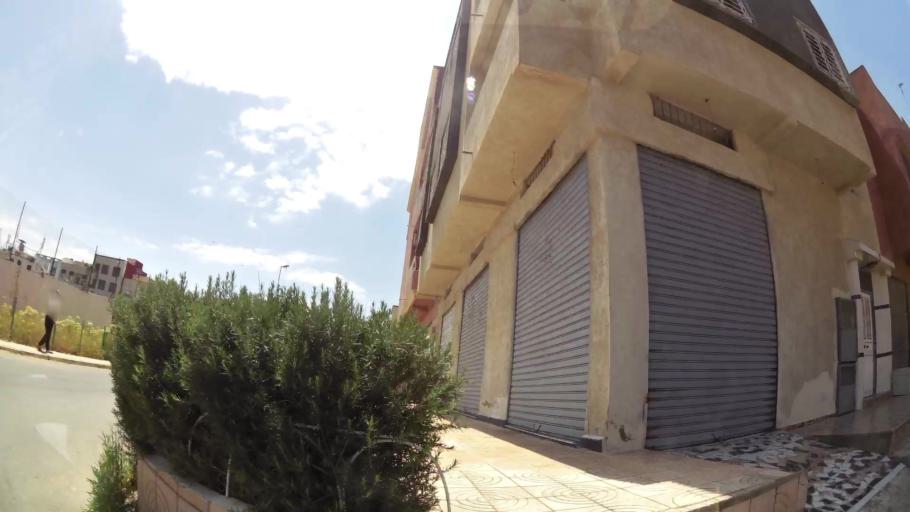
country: MA
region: Gharb-Chrarda-Beni Hssen
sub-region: Kenitra Province
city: Kenitra
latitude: 34.2703
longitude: -6.6172
